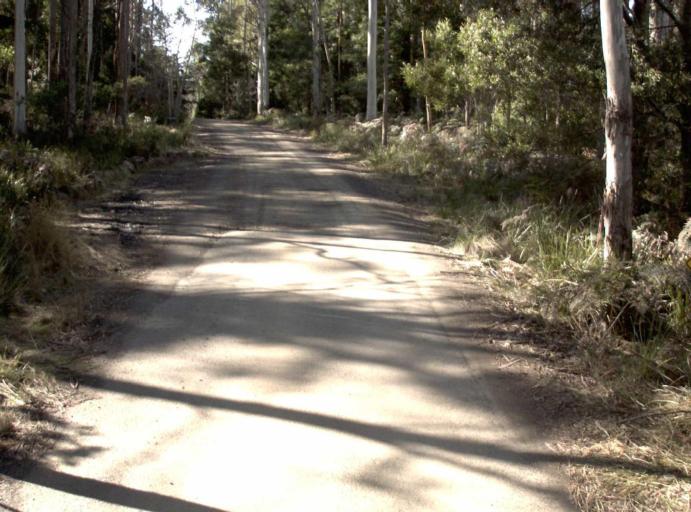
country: AU
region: Tasmania
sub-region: Launceston
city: Mayfield
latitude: -41.3096
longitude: 147.2060
